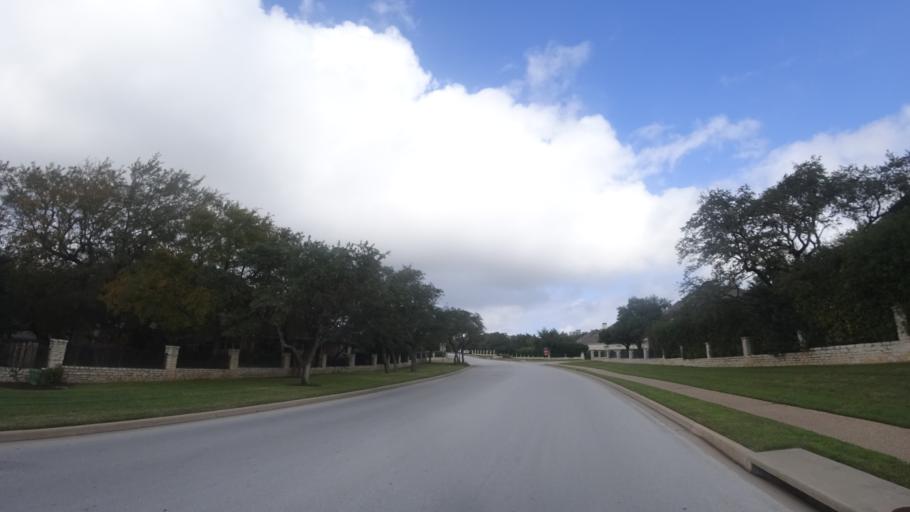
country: US
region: Texas
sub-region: Travis County
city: Barton Creek
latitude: 30.3104
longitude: -97.8972
